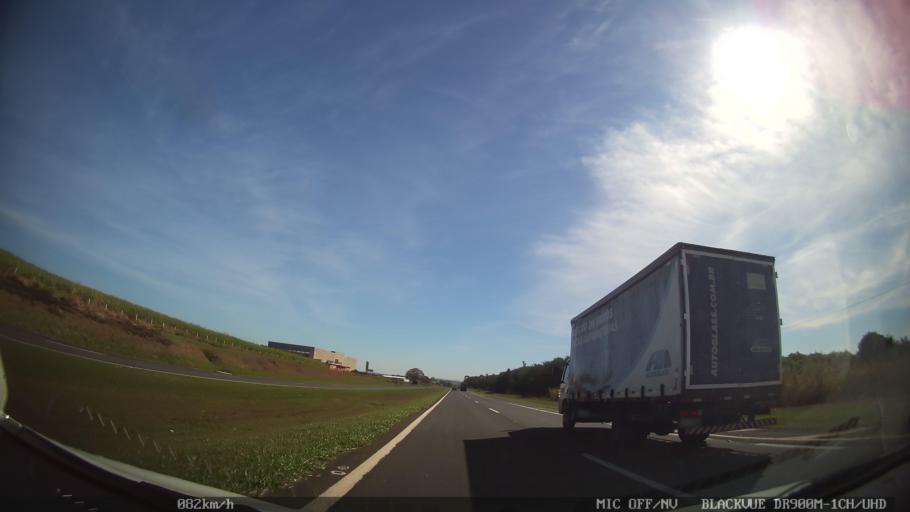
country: BR
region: Sao Paulo
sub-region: Leme
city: Leme
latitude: -22.1417
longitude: -47.4035
